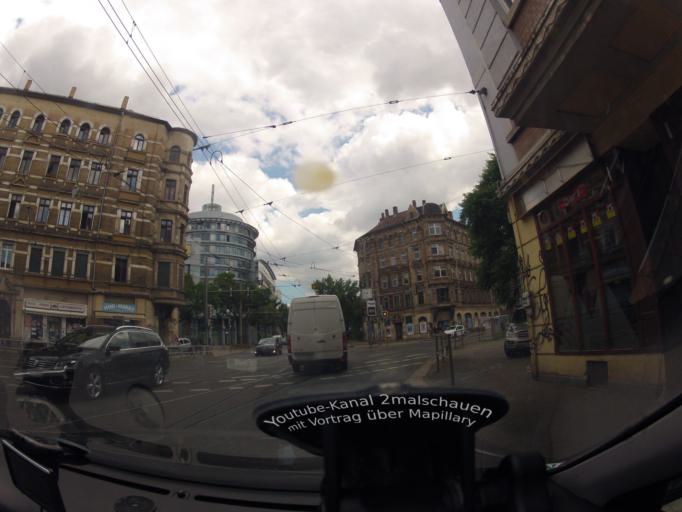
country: DE
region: Saxony
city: Leipzig
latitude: 51.3449
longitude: 12.4142
